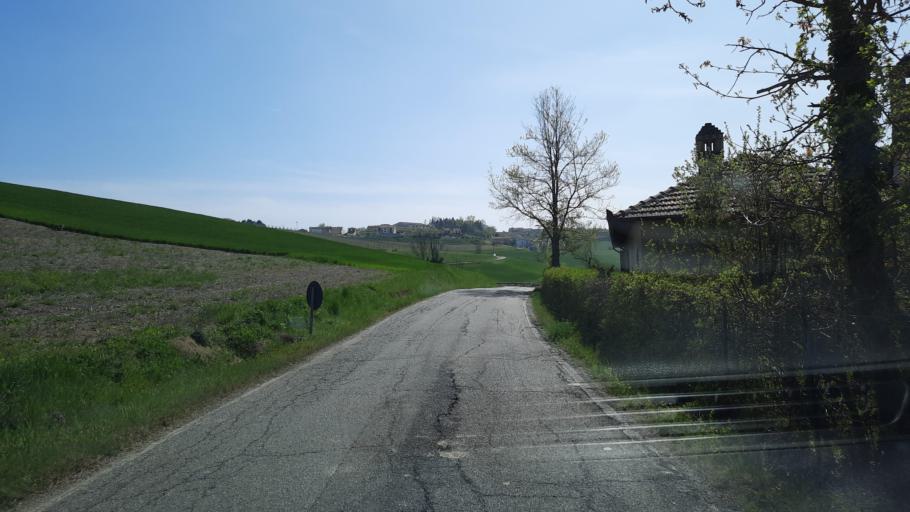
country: IT
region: Piedmont
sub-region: Provincia di Alessandria
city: Sala Monferrato
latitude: 45.0826
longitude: 8.3652
